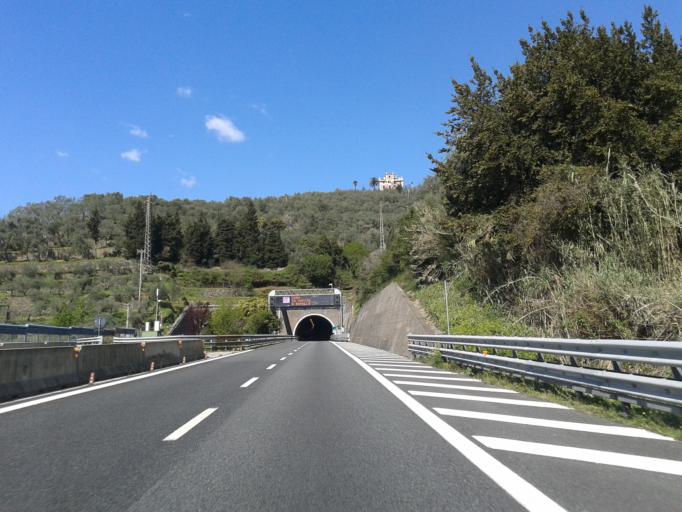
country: IT
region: Liguria
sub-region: Provincia di Genova
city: Chiavari
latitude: 44.3233
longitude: 9.3355
